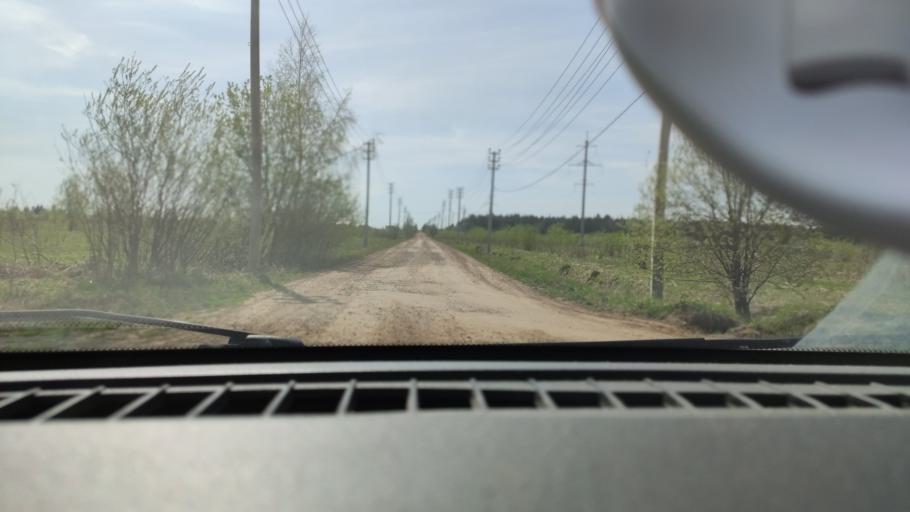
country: RU
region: Perm
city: Kultayevo
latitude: 57.8901
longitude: 55.8635
